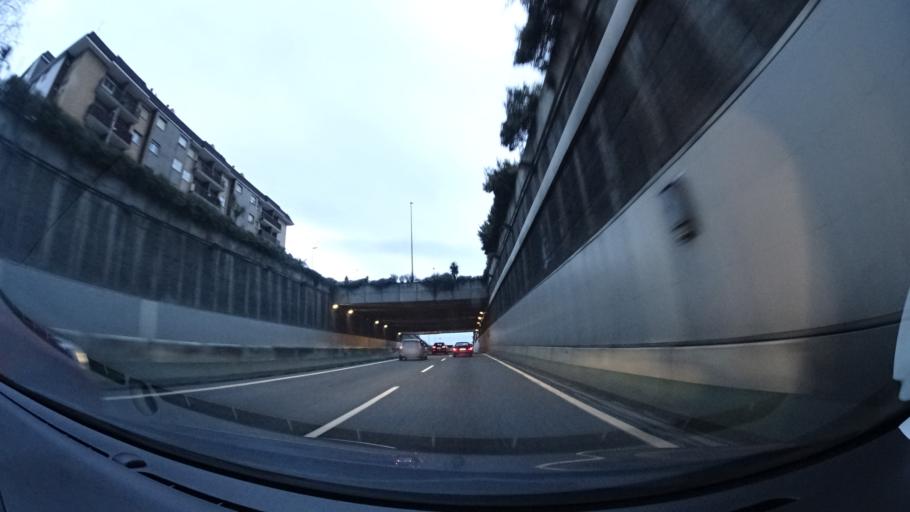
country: ES
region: Basque Country
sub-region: Bizkaia
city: Leioa
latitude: 43.3275
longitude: -2.9905
